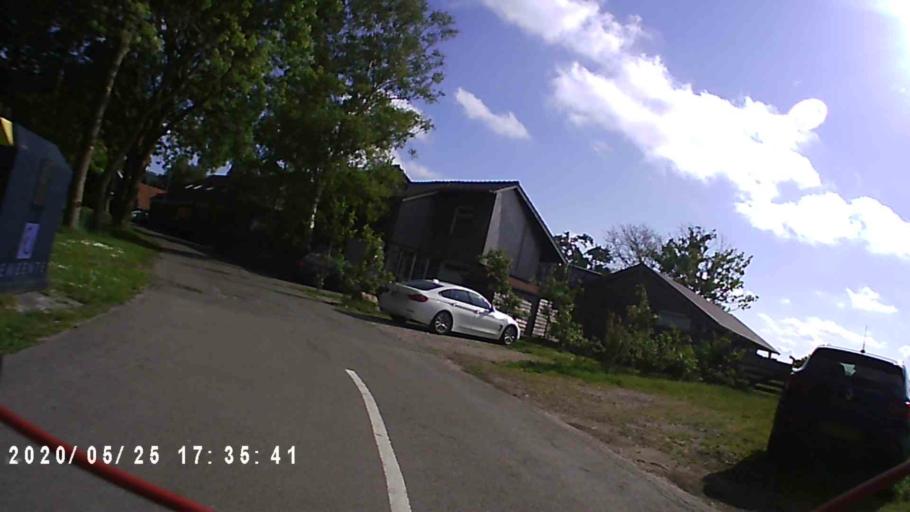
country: NL
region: Groningen
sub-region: Gemeente Groningen
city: Korrewegwijk
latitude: 53.2431
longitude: 6.5674
